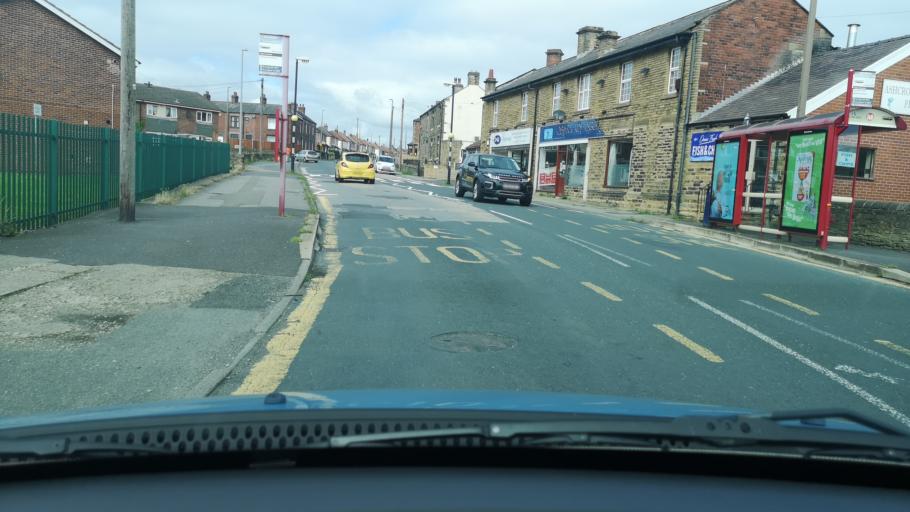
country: GB
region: England
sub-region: Kirklees
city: Mirfield
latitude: 53.6880
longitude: -1.6911
